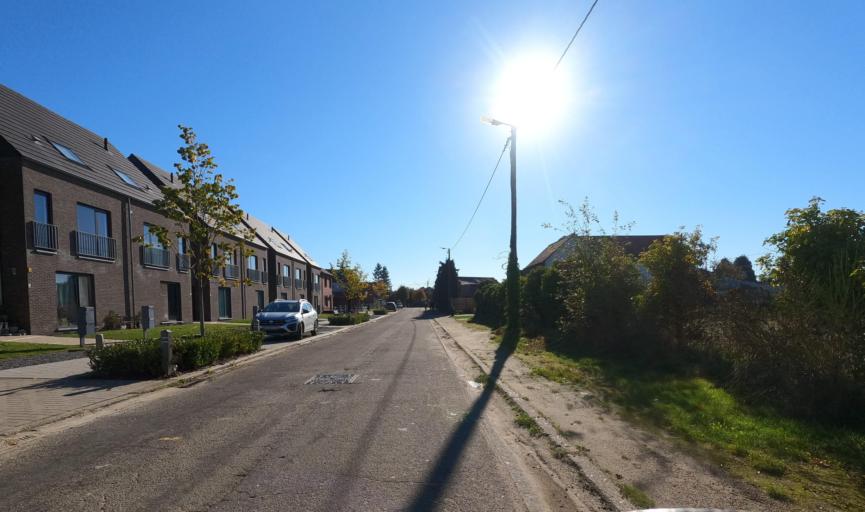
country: BE
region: Flanders
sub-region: Provincie Antwerpen
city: Hulshout
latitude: 51.1051
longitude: 4.7867
